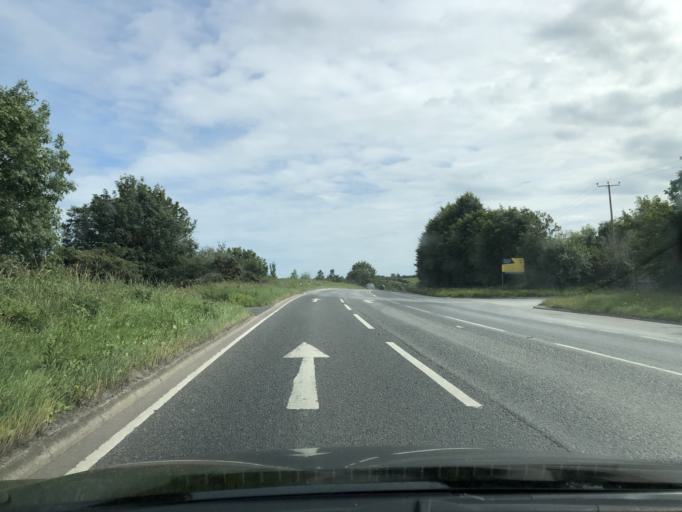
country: GB
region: Northern Ireland
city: Ballynahinch
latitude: 54.3389
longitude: -5.8387
